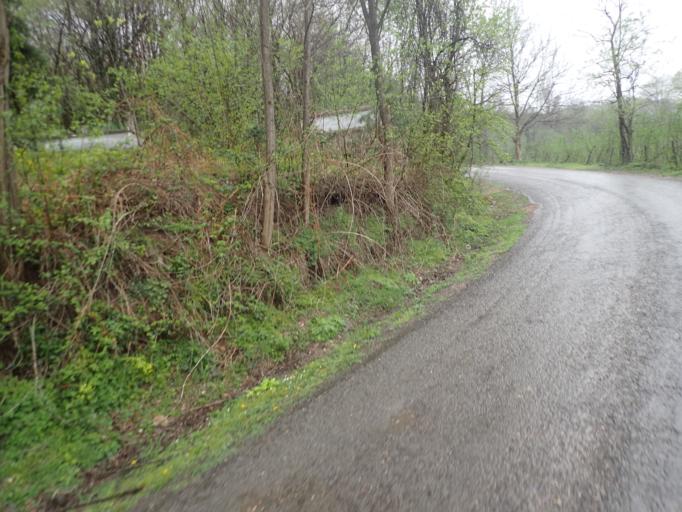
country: TR
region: Ordu
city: Korgan
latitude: 40.7835
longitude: 37.3449
